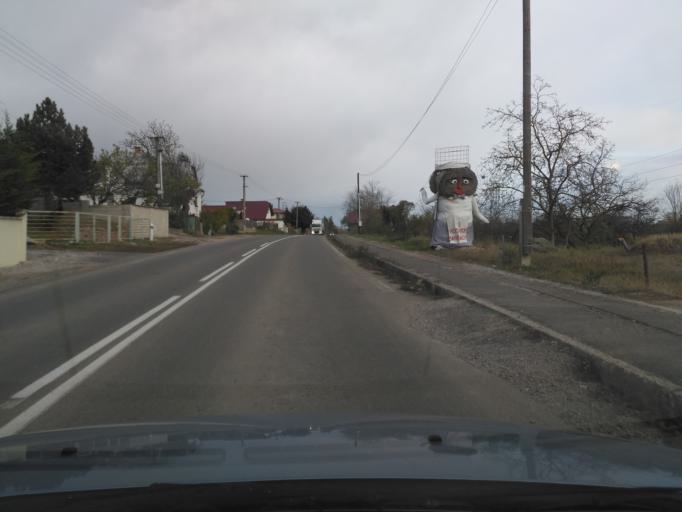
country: HU
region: Borsod-Abauj-Zemplen
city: Satoraljaujhely
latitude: 48.3973
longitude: 21.7302
